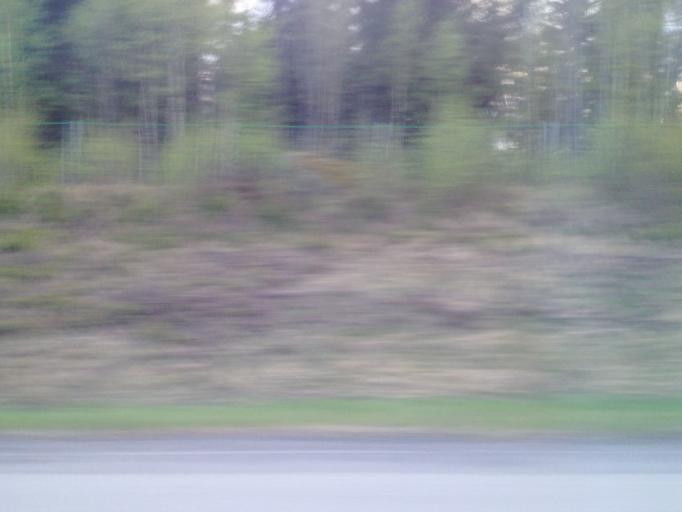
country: FI
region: Pirkanmaa
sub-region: Etelae-Pirkanmaa
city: Valkeakoski
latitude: 61.1514
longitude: 23.9881
